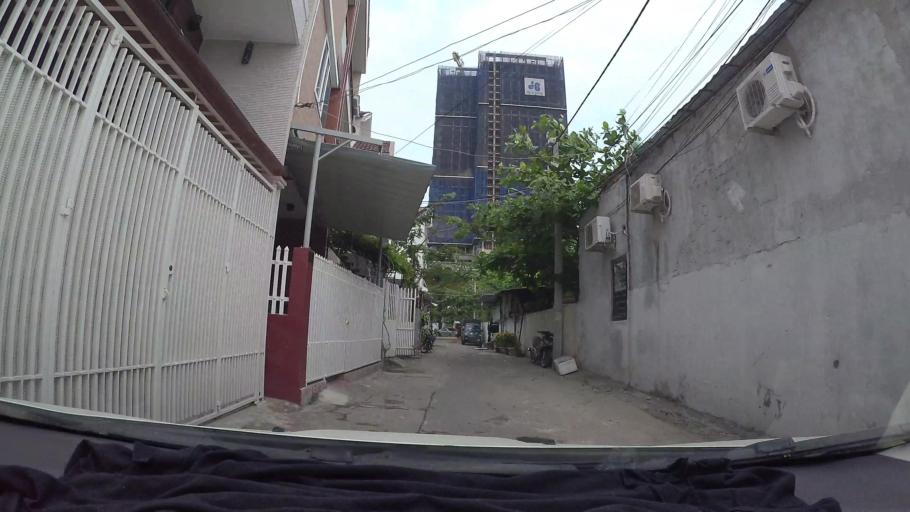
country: VN
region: Da Nang
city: Da Nang
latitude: 16.0854
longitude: 108.2216
